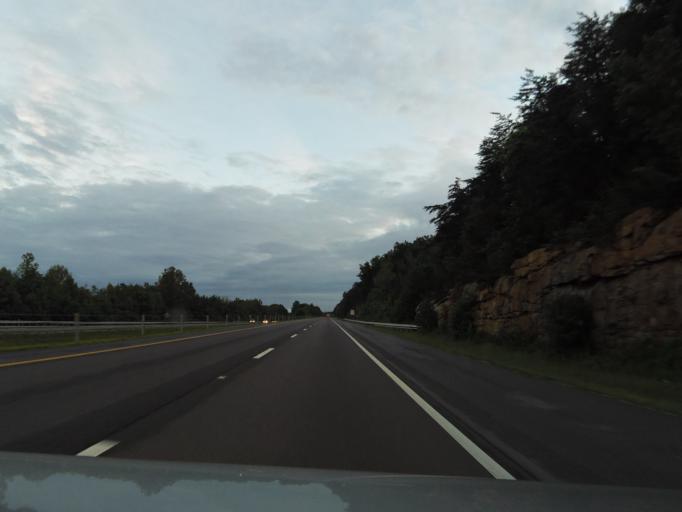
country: US
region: Tennessee
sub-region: Campbell County
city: Jellico
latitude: 36.4880
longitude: -84.2162
